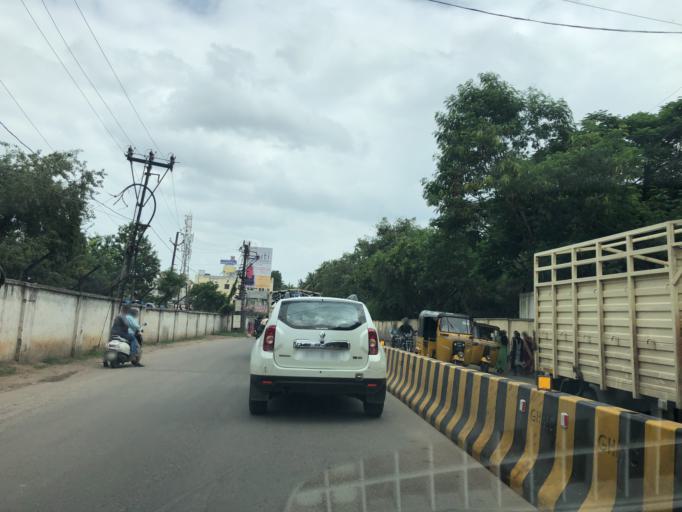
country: IN
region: Telangana
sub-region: Rangareddi
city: Quthbullapur
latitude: 17.4698
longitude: 78.4764
